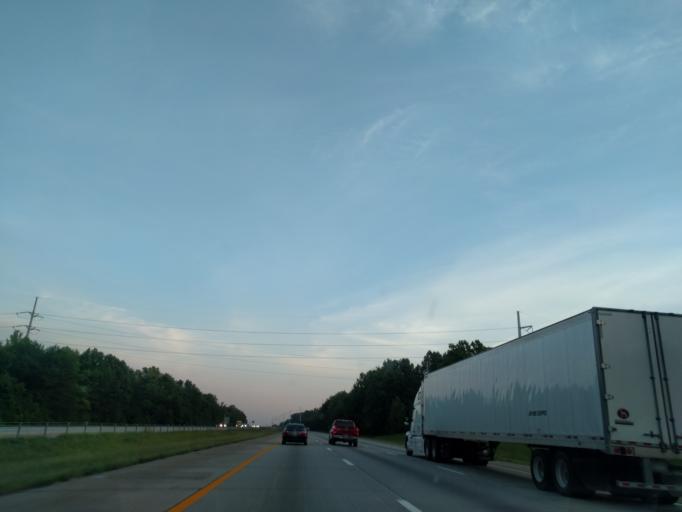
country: US
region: Kentucky
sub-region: Bullitt County
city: Hillview
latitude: 38.0906
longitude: -85.7011
